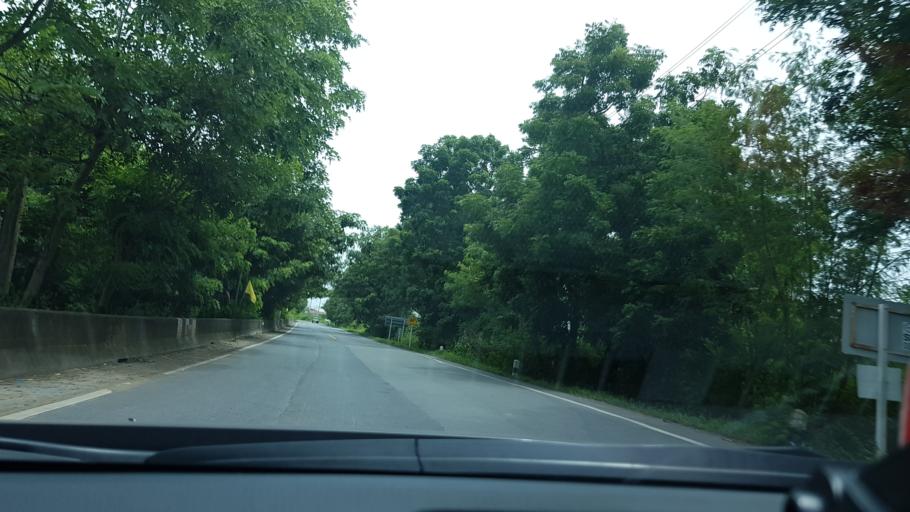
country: TH
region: Pathum Thani
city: Sam Khok
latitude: 14.1403
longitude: 100.5297
